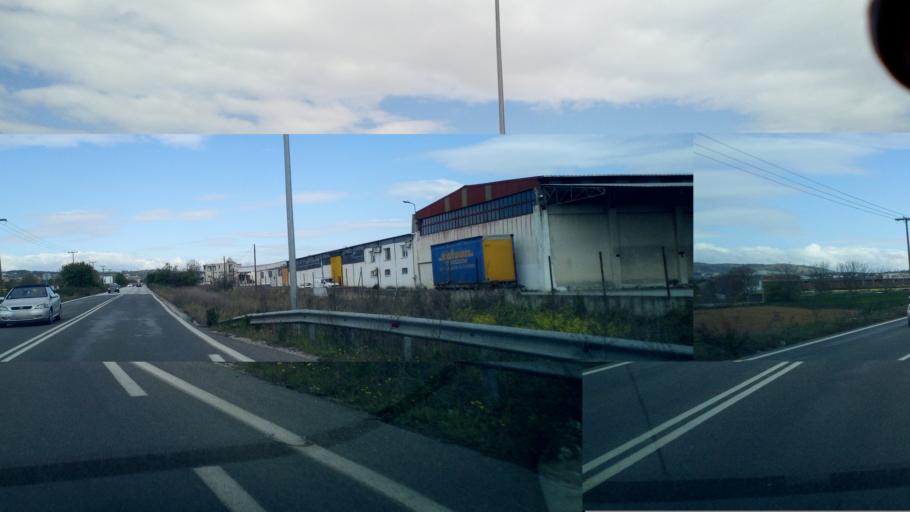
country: GR
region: Central Macedonia
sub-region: Nomos Thessalonikis
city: Liti
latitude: 40.7613
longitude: 22.9683
